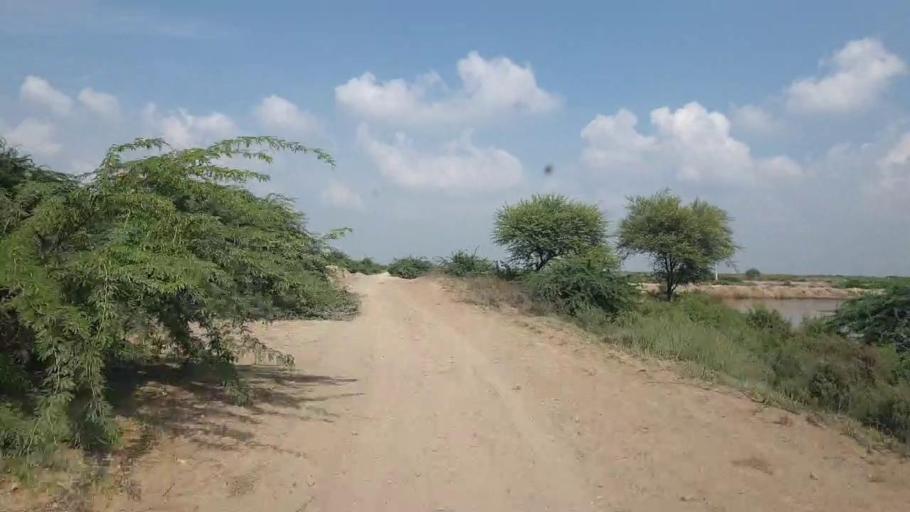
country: PK
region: Sindh
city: Badin
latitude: 24.4942
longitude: 68.6559
